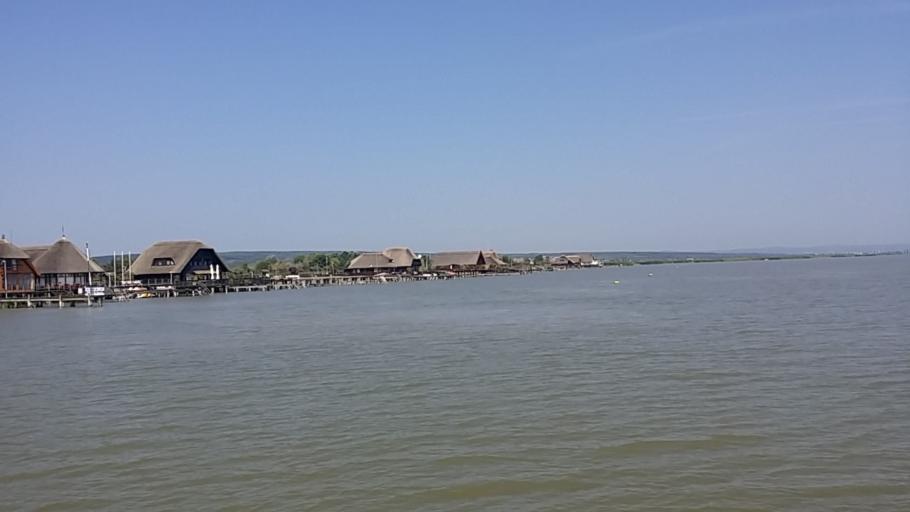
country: AT
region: Burgenland
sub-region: Eisenstadt-Umgebung
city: Morbisch am See
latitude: 47.7208
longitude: 16.6937
